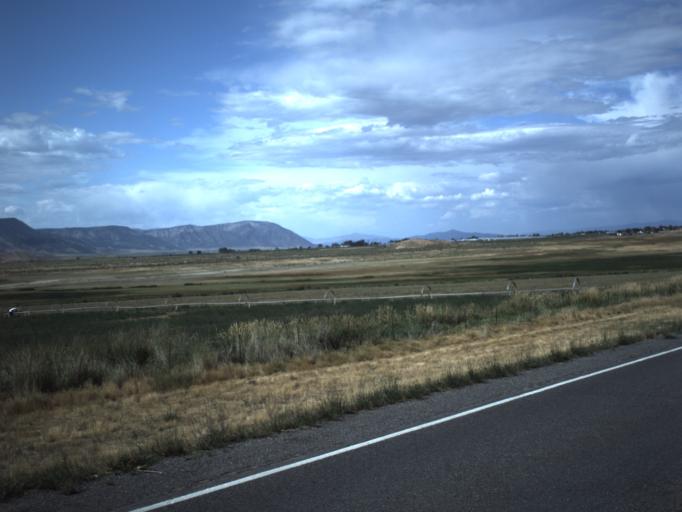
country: US
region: Utah
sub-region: Sanpete County
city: Manti
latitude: 39.2297
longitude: -111.6687
